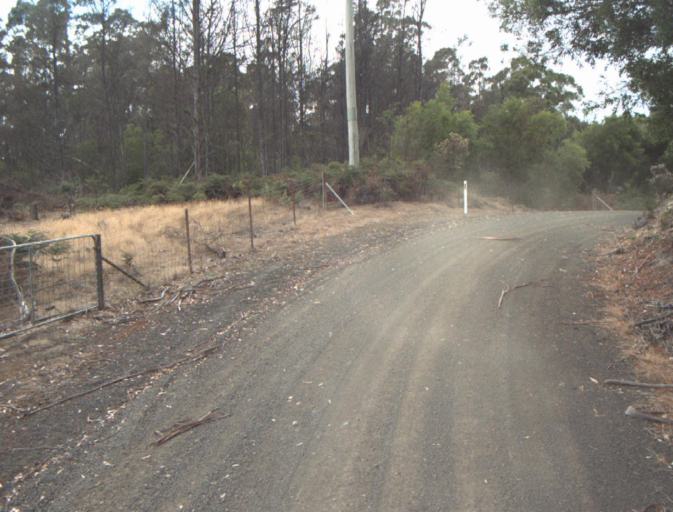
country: AU
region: Tasmania
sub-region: Launceston
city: Mayfield
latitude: -41.1983
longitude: 147.2304
